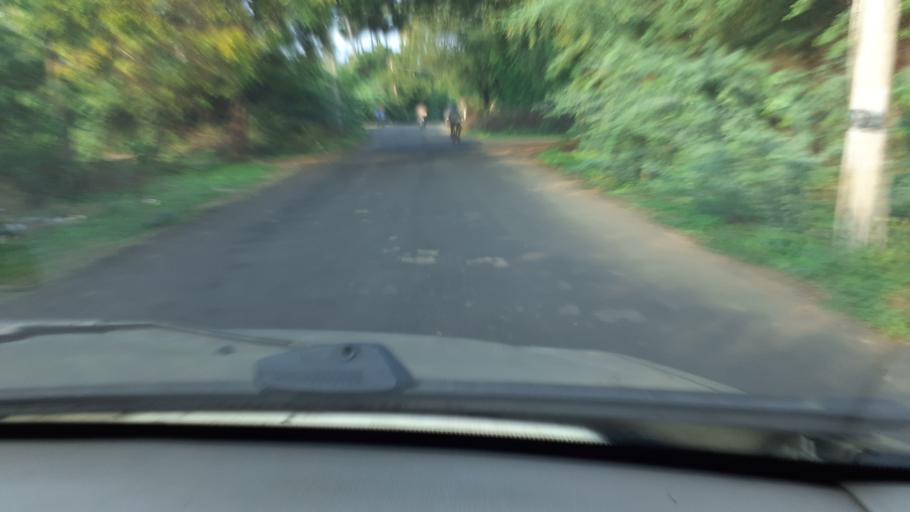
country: IN
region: Tamil Nadu
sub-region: Thoothukkudi
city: Alwar Tirunagari
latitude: 8.6014
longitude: 77.9759
